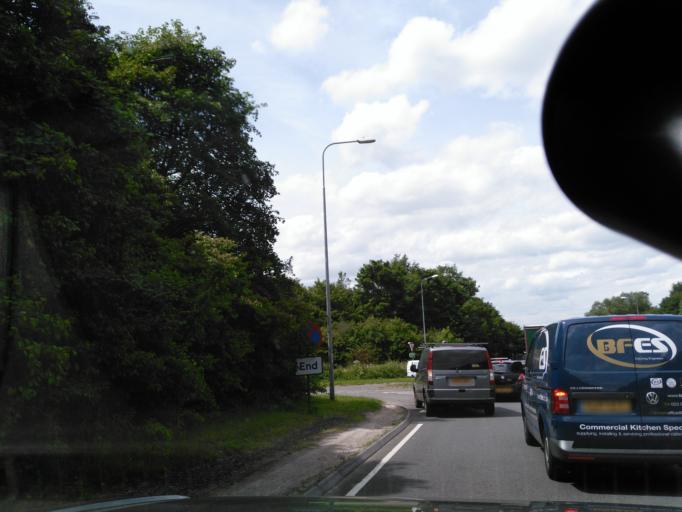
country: GB
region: England
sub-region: Wiltshire
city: Alderbury
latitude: 51.0588
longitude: -1.7590
